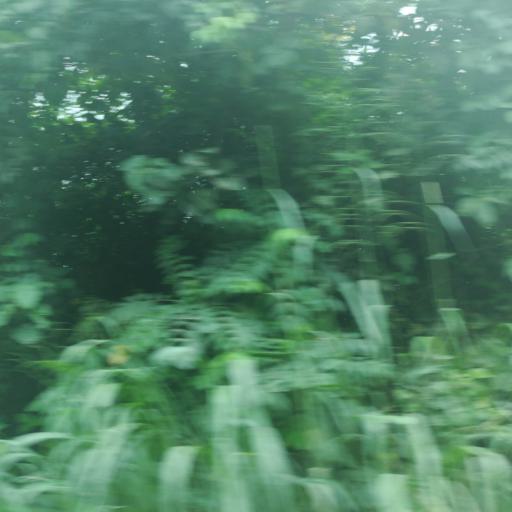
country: NG
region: Lagos
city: Ejirin
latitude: 6.6441
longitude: 3.8519
